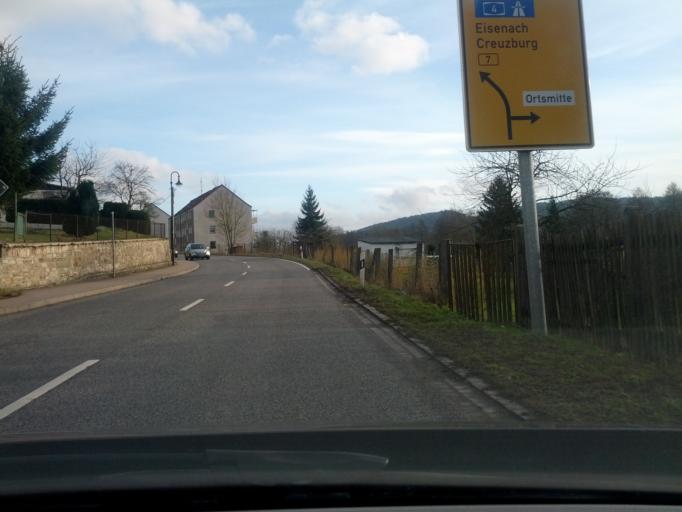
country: DE
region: Thuringia
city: Ifta
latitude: 51.0684
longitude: 10.1722
